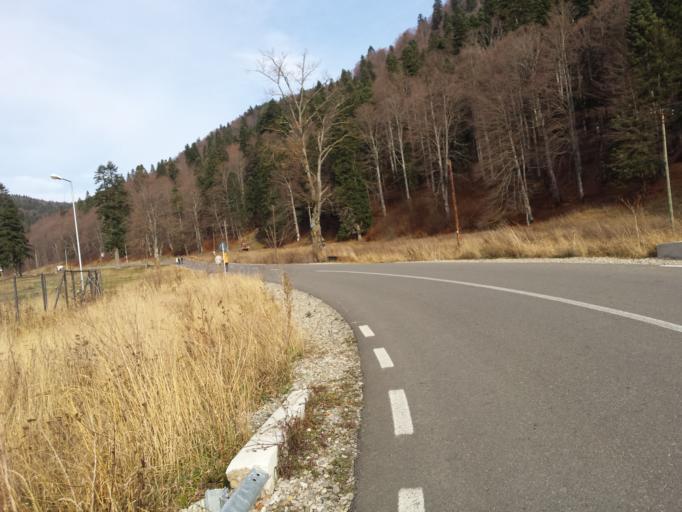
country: RO
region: Prahova
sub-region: Oras Azuga
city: Azuga
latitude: 45.4426
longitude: 25.5252
